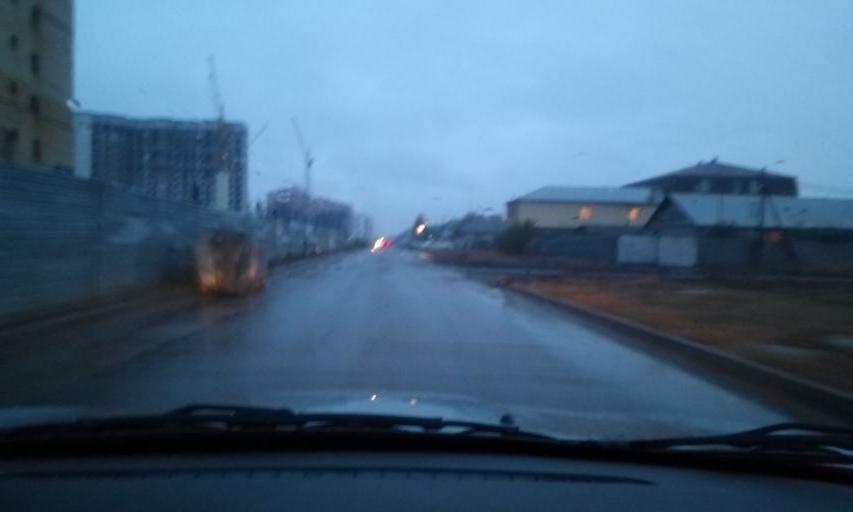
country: KZ
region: Astana Qalasy
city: Astana
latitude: 51.1921
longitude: 71.3373
